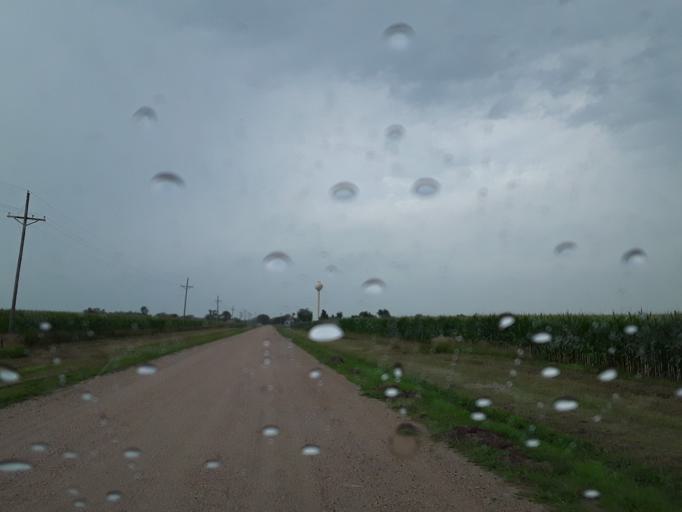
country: US
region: Nebraska
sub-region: Saunders County
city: Yutan
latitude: 41.1790
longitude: -96.4449
